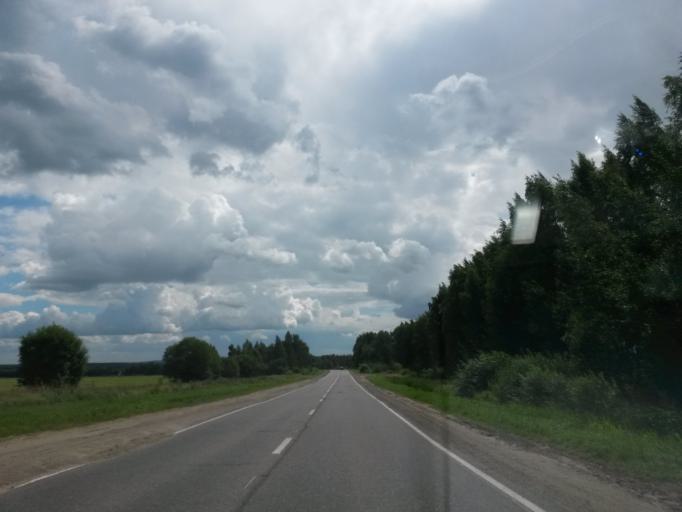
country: RU
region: Jaroslavl
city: Yaroslavl
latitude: 57.5397
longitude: 39.8667
